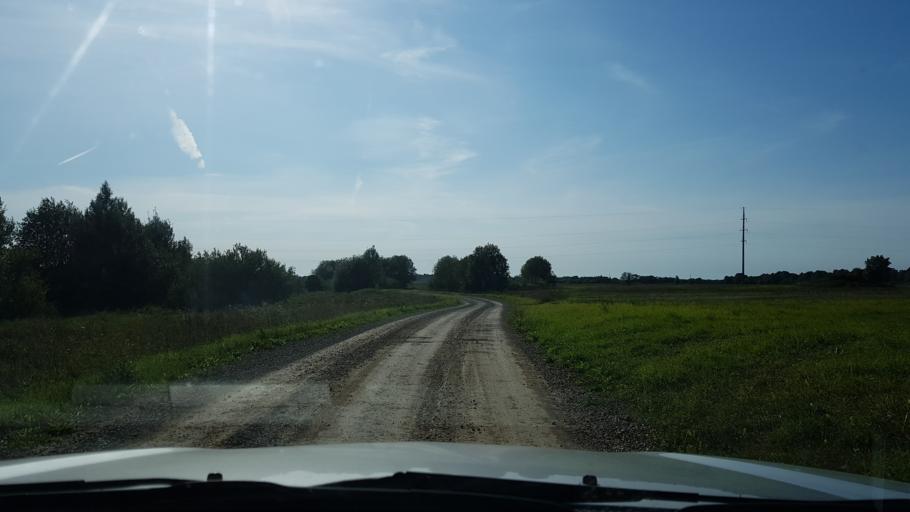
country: EE
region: Ida-Virumaa
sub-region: Narva-Joesuu linn
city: Narva-Joesuu
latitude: 59.4095
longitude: 28.0145
